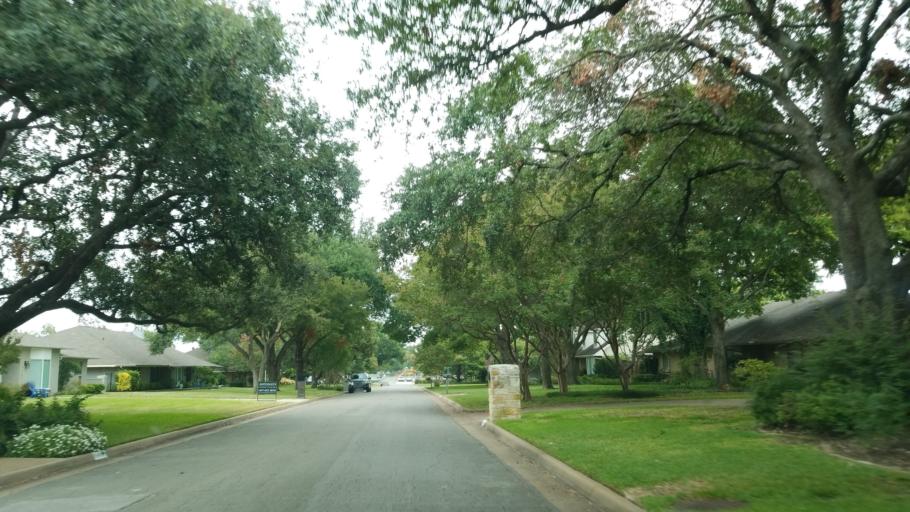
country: US
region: Texas
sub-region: Dallas County
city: Addison
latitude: 32.9475
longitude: -96.7809
